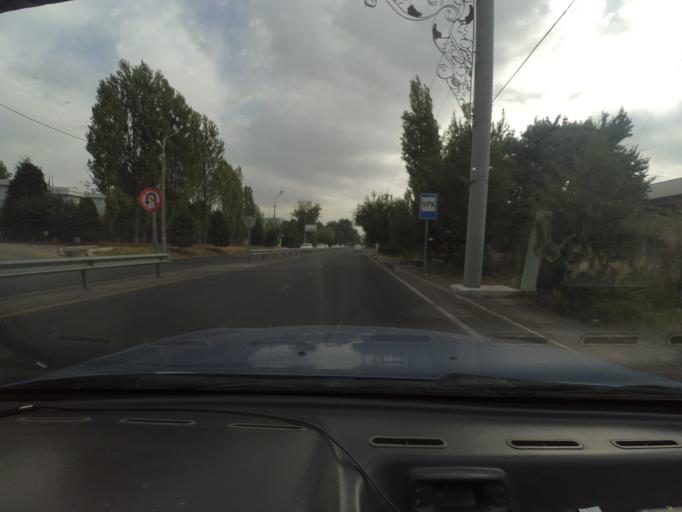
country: UZ
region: Toshkent
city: Qibray
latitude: 41.3808
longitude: 69.4424
